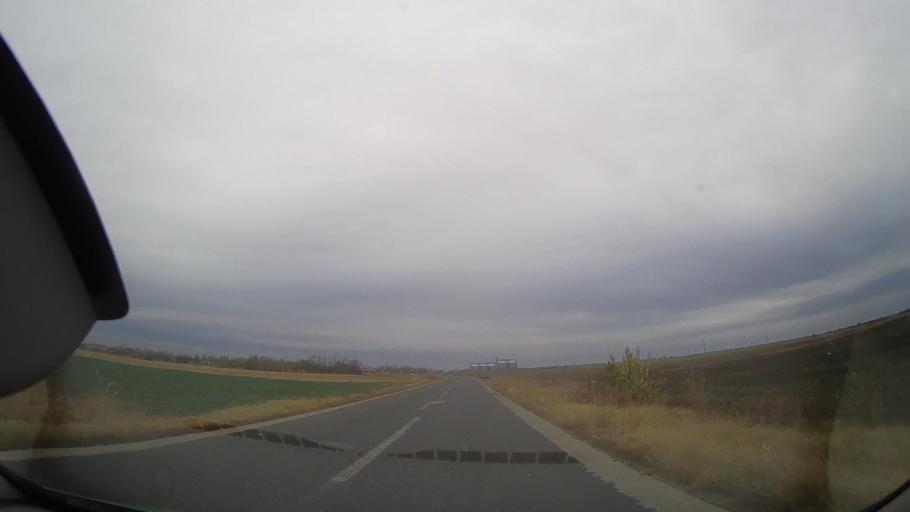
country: RO
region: Ialomita
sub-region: Comuna Milosesti
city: Milosesti
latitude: 44.7592
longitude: 27.2002
